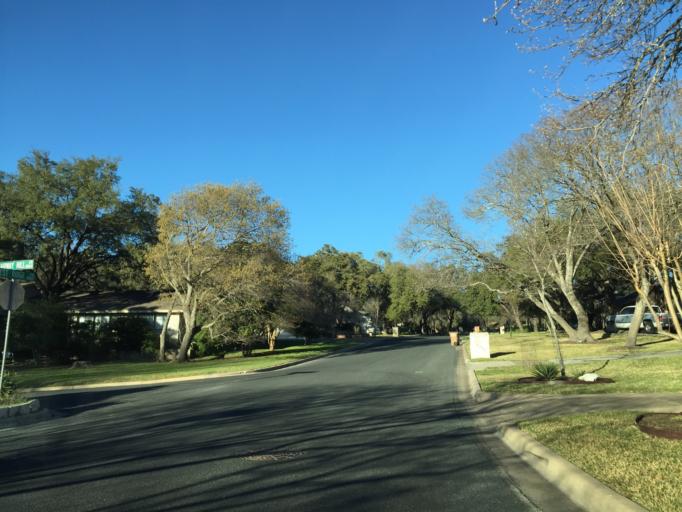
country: US
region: Texas
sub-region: Williamson County
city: Jollyville
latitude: 30.4363
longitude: -97.7879
